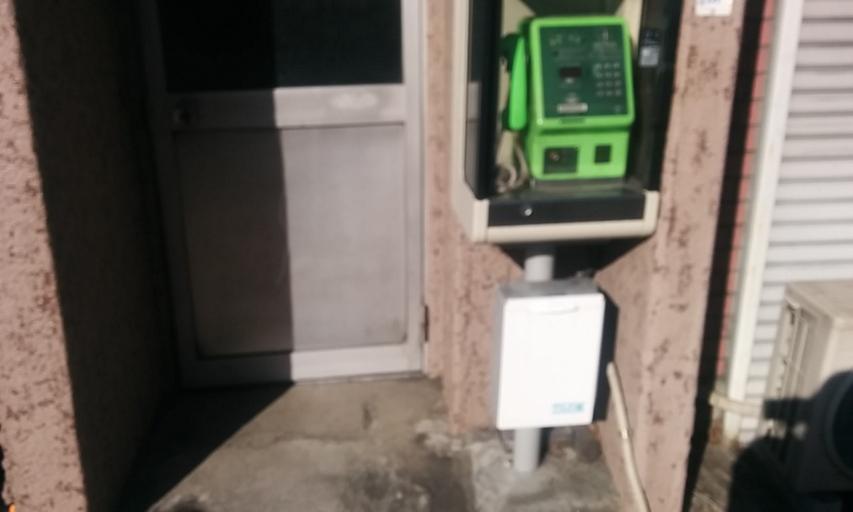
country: JP
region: Tokyo
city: Urayasu
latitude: 35.7111
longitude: 139.8045
